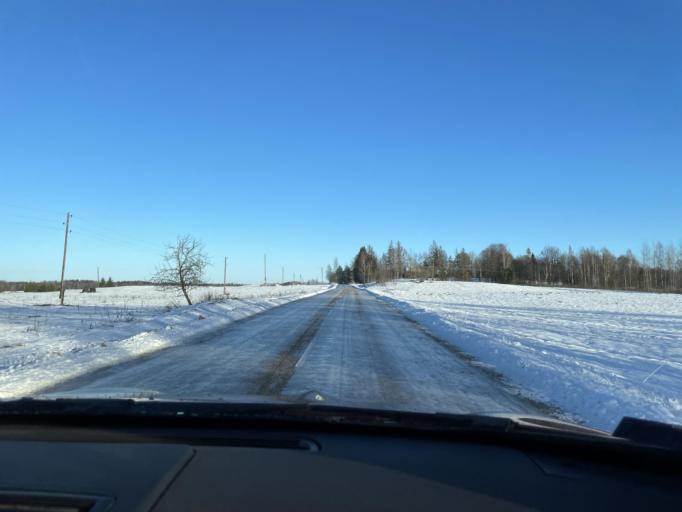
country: LV
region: Ludzas Rajons
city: Ludza
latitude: 56.4514
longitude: 27.5526
